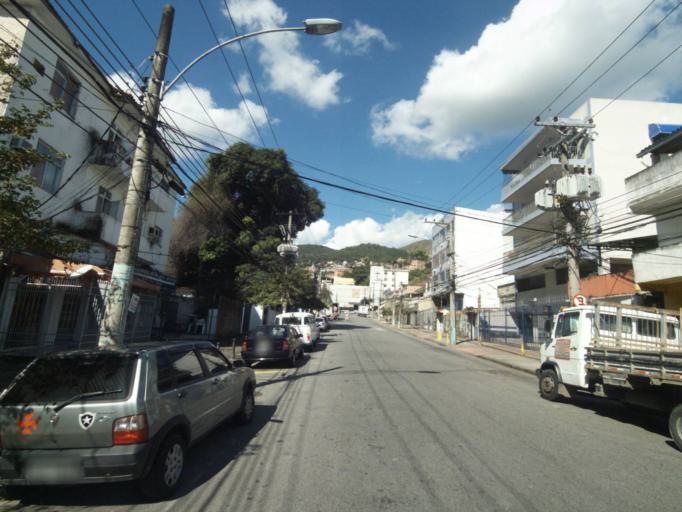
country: BR
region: Rio de Janeiro
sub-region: Rio De Janeiro
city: Rio de Janeiro
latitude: -22.9109
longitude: -43.2870
